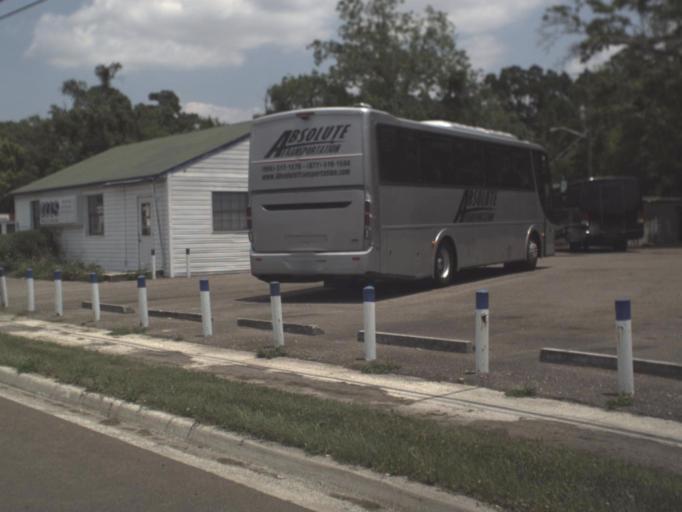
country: US
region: Florida
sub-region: Duval County
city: Jacksonville
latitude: 30.2880
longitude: -81.7303
